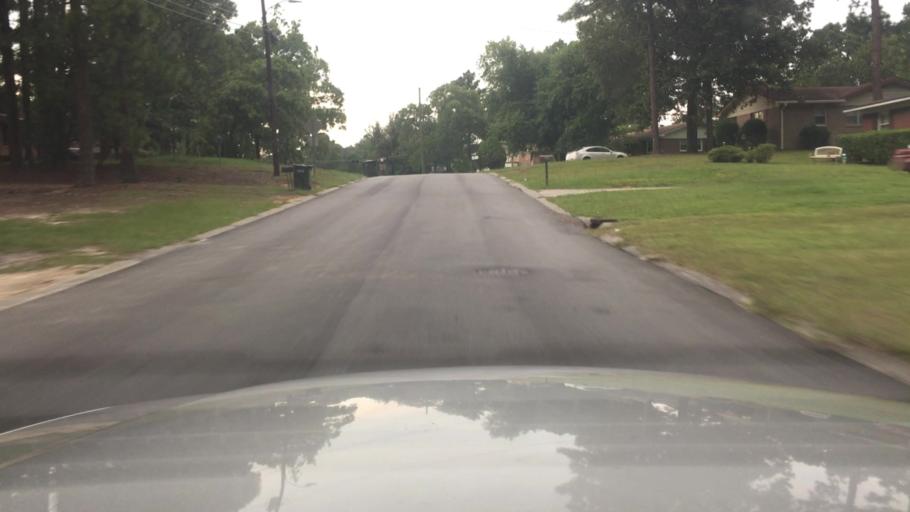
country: US
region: North Carolina
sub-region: Cumberland County
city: Fort Bragg
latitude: 35.0965
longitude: -79.0179
